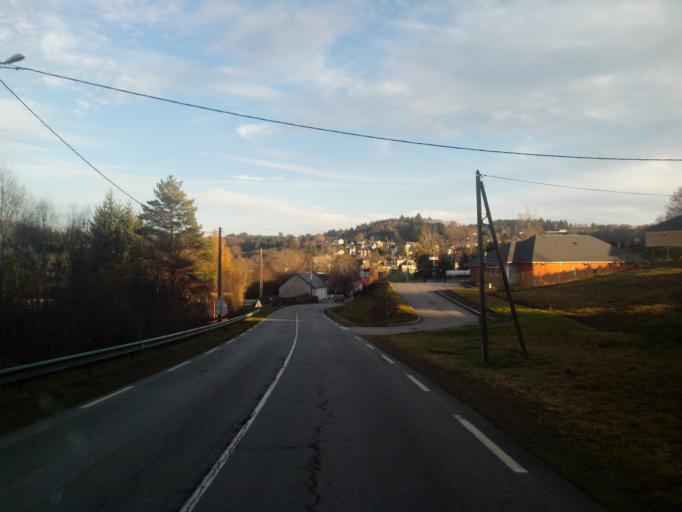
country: FR
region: Limousin
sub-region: Departement de la Correze
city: Bugeat
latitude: 45.6020
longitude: 1.9183
